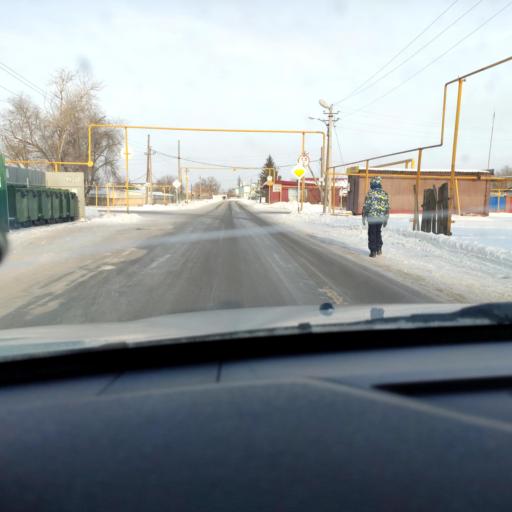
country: RU
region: Samara
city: Smyshlyayevka
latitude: 53.1616
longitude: 50.3825
